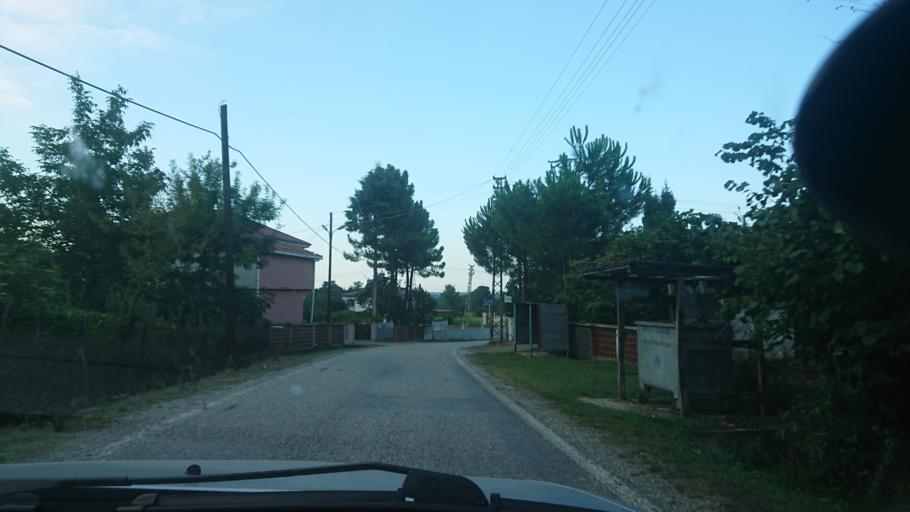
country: TR
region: Samsun
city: Dikbiyik
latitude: 41.1754
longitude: 36.5423
